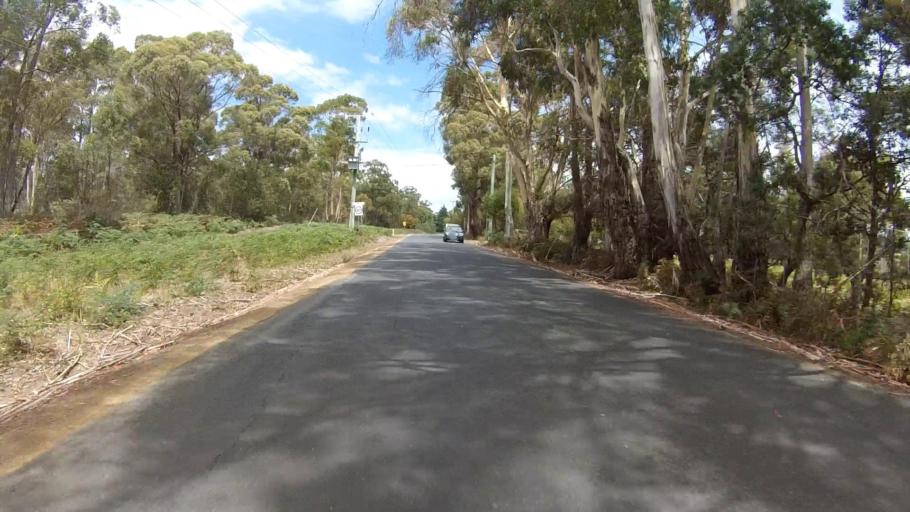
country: AU
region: Tasmania
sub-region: Kingborough
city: Blackmans Bay
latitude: -43.0103
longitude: 147.2881
